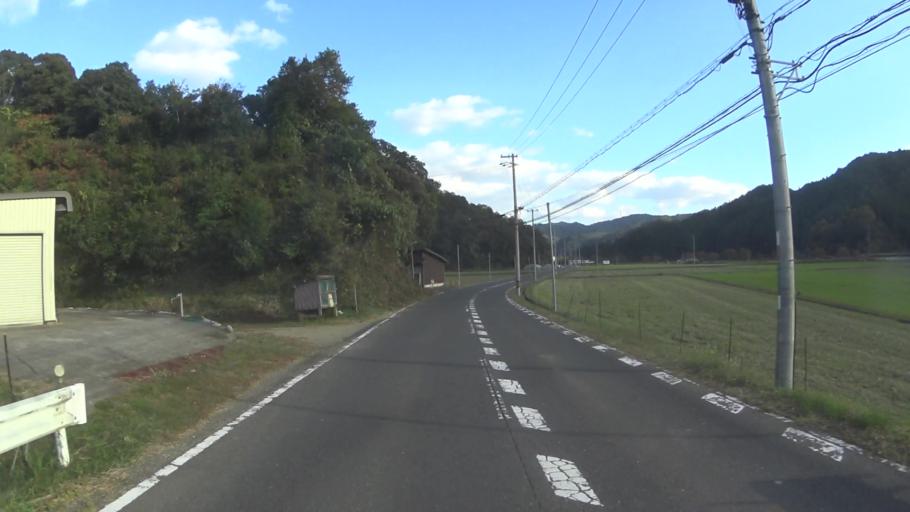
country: JP
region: Kyoto
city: Miyazu
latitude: 35.4372
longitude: 135.2225
